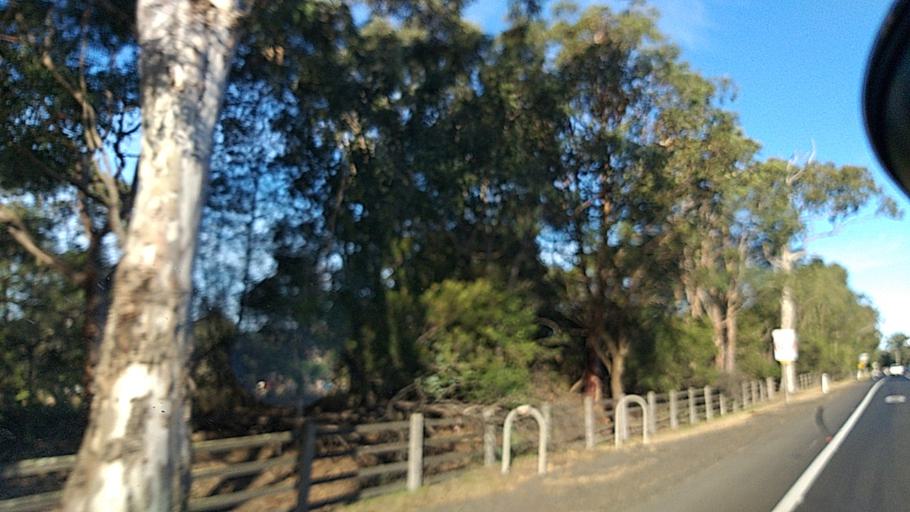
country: AU
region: New South Wales
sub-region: Hawkesbury
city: South Windsor
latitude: -33.6570
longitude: 150.7951
